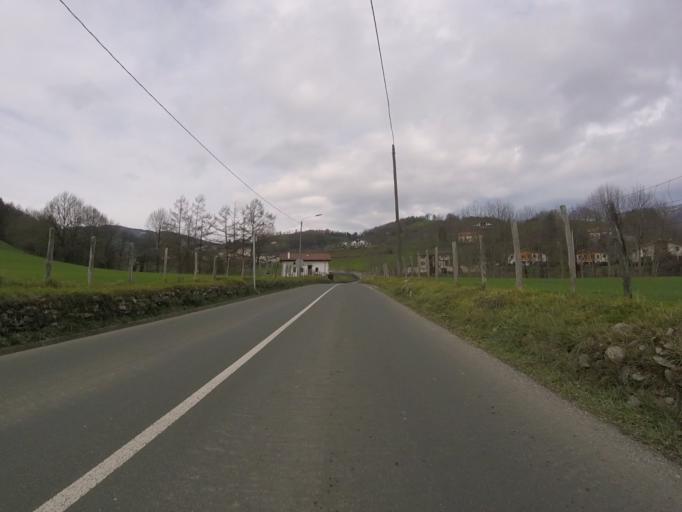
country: ES
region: Basque Country
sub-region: Provincia de Guipuzcoa
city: Errezil
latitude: 43.1401
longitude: -2.1628
